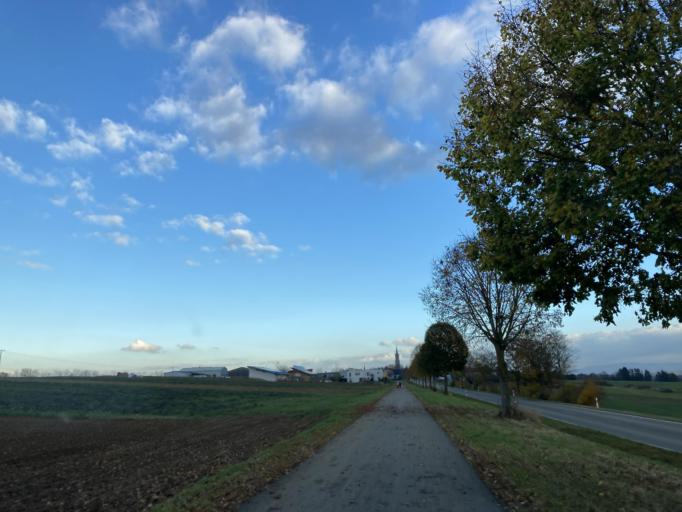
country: DE
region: Baden-Wuerttemberg
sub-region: Tuebingen Region
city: Haigerloch
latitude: 48.4321
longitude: 8.8006
